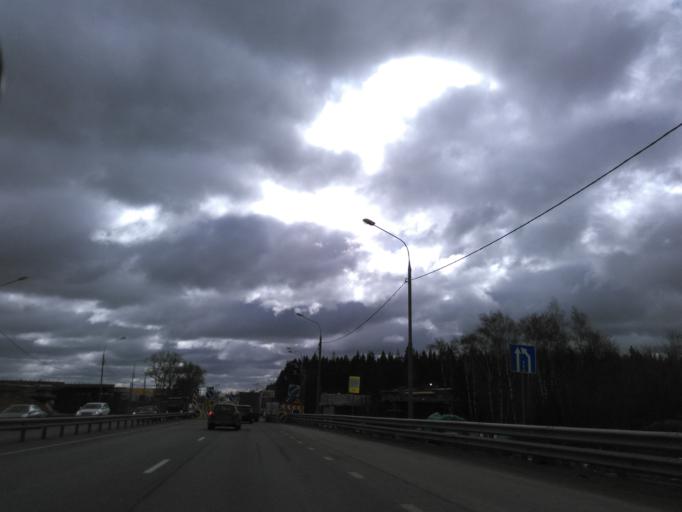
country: RU
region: Moskovskaya
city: Rzhavki
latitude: 55.9943
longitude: 37.2586
